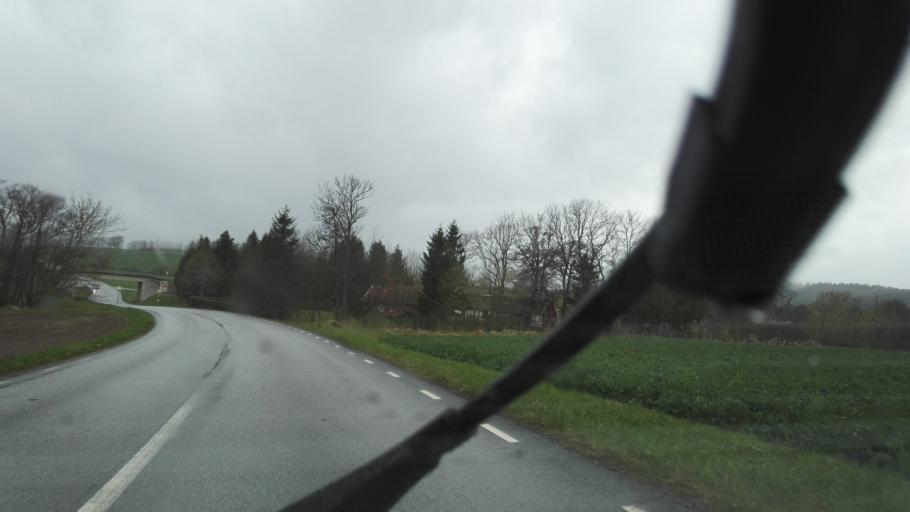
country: SE
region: Skane
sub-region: Simrishamns Kommun
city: Kivik
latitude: 55.7177
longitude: 14.1437
